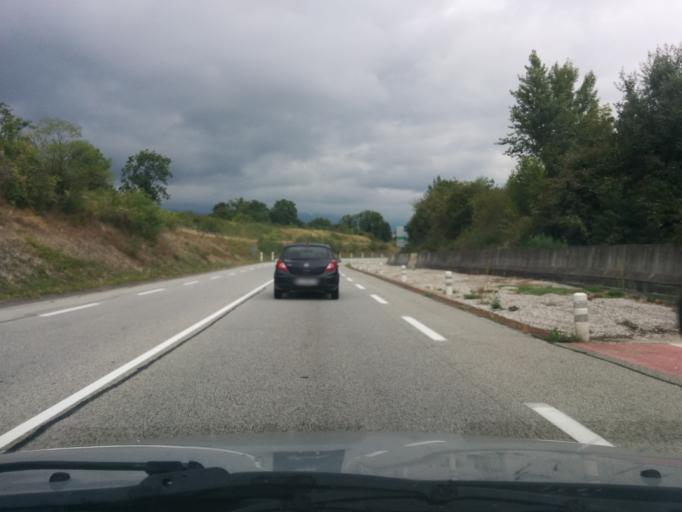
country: FR
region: Rhone-Alpes
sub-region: Departement de l'Isere
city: Voiron
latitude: 45.3823
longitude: 5.5740
